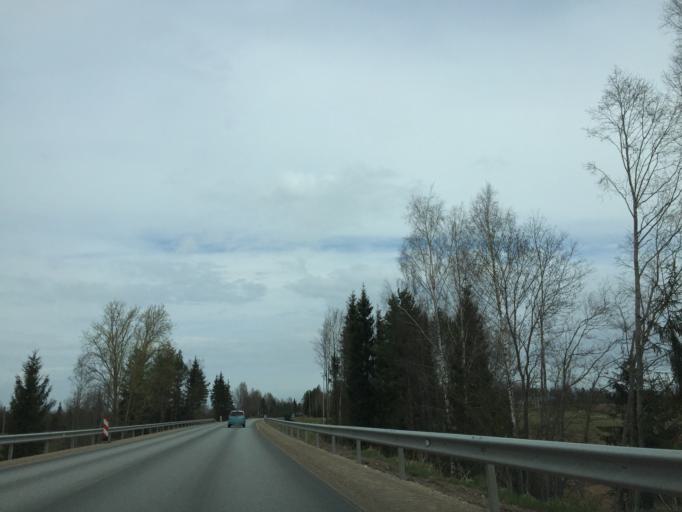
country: LV
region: Amatas Novads
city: Drabesi
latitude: 57.2318
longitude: 25.2538
